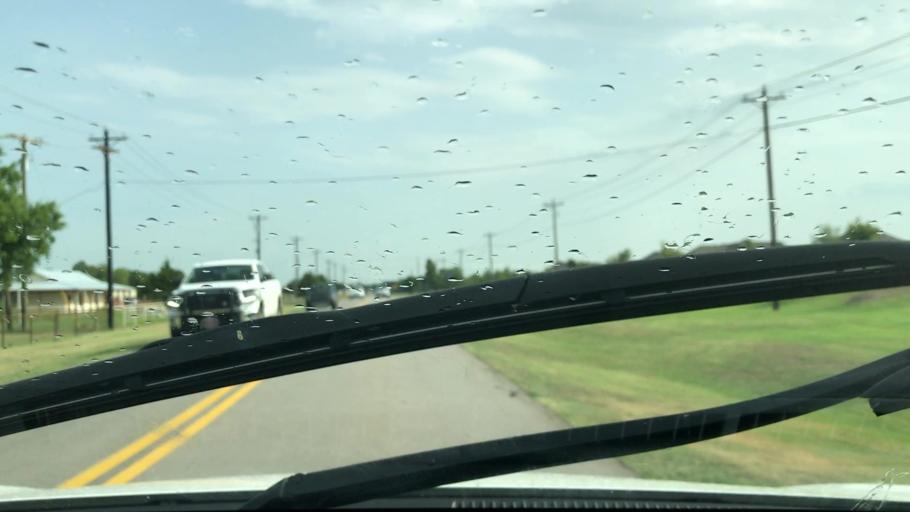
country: US
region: Texas
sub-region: Collin County
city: Wylie
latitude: 32.9860
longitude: -96.5218
